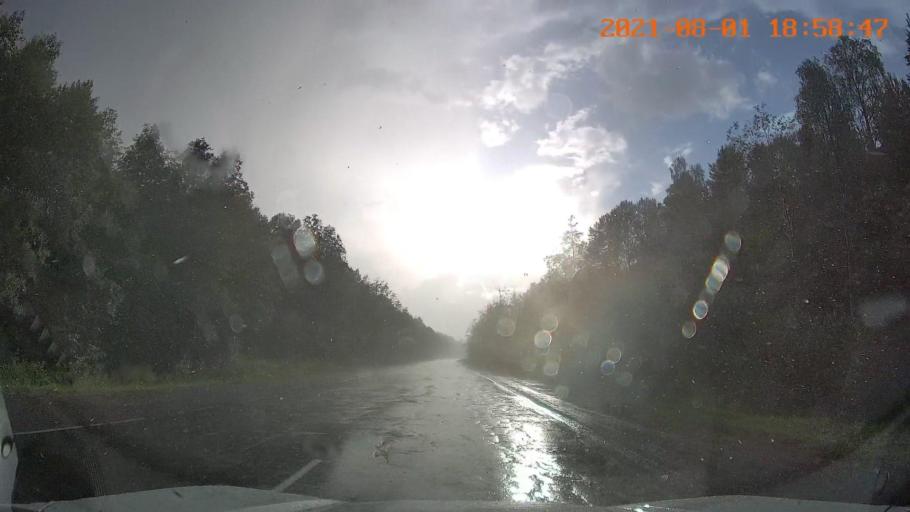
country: RU
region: Leningrad
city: Podporozh'ye
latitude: 60.9004
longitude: 34.6777
